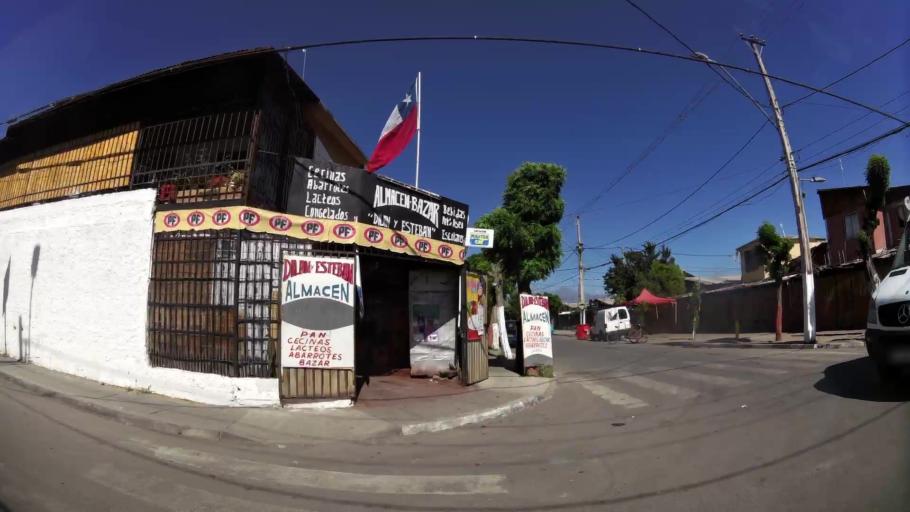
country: CL
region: Santiago Metropolitan
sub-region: Provincia de Maipo
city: San Bernardo
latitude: -33.5857
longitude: -70.6677
